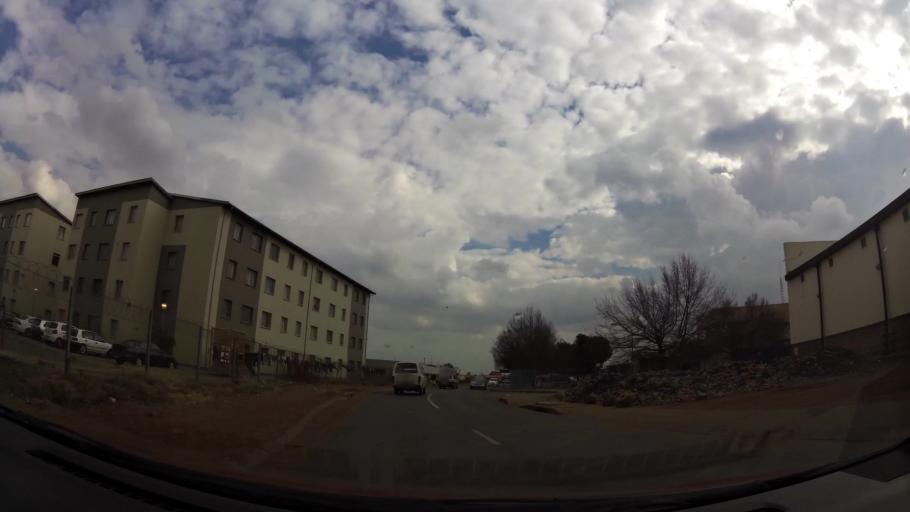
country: ZA
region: Gauteng
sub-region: City of Johannesburg Metropolitan Municipality
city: Soweto
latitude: -26.2519
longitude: 27.8559
